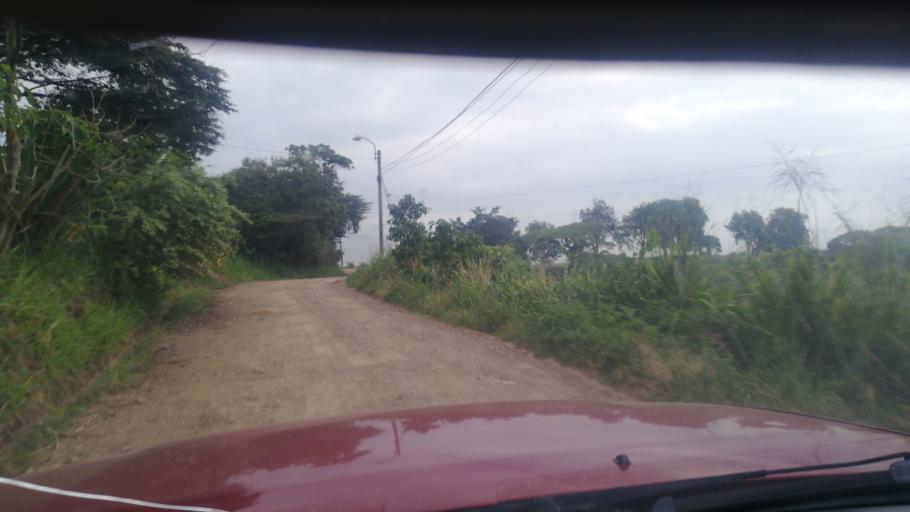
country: CO
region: Valle del Cauca
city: Cali
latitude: 3.5082
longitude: -76.5421
